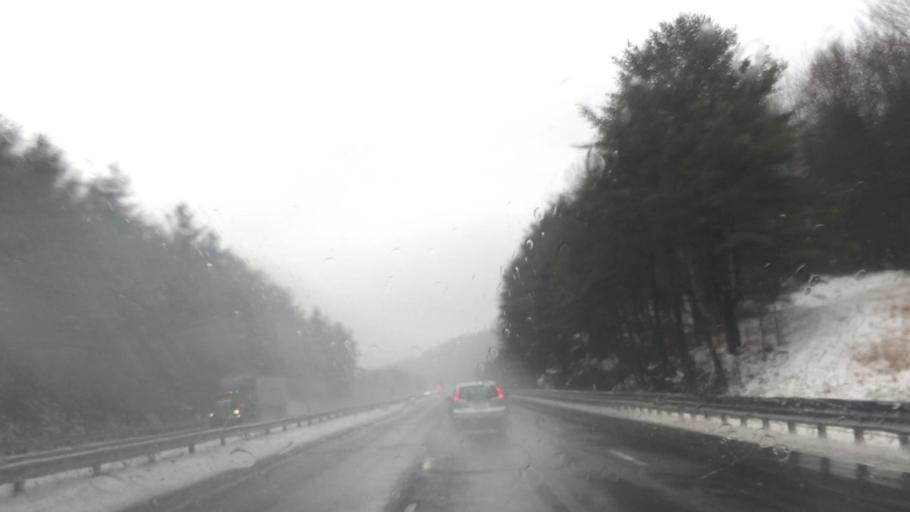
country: US
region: Massachusetts
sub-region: Hampden County
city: Granville
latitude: 42.1694
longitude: -72.8711
